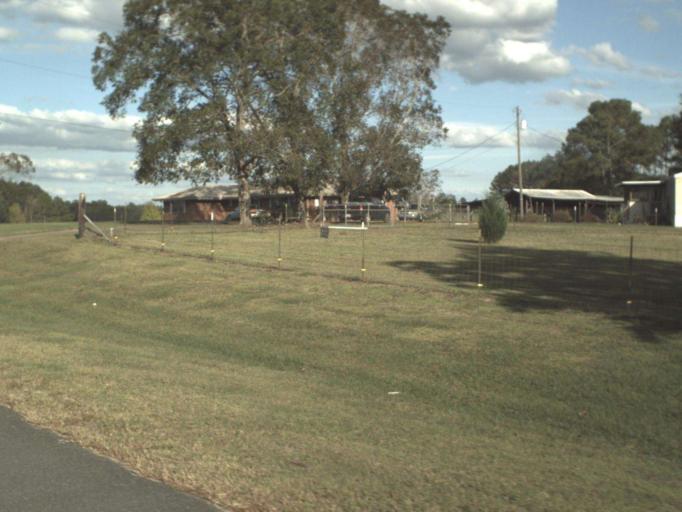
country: US
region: Florida
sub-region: Washington County
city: Chipley
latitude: 30.7578
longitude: -85.5787
